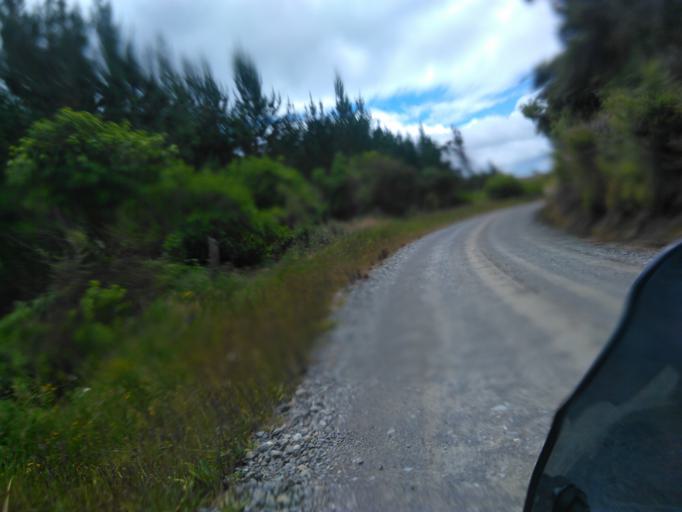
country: NZ
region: Gisborne
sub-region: Gisborne District
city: Gisborne
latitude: -38.1809
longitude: 178.1241
